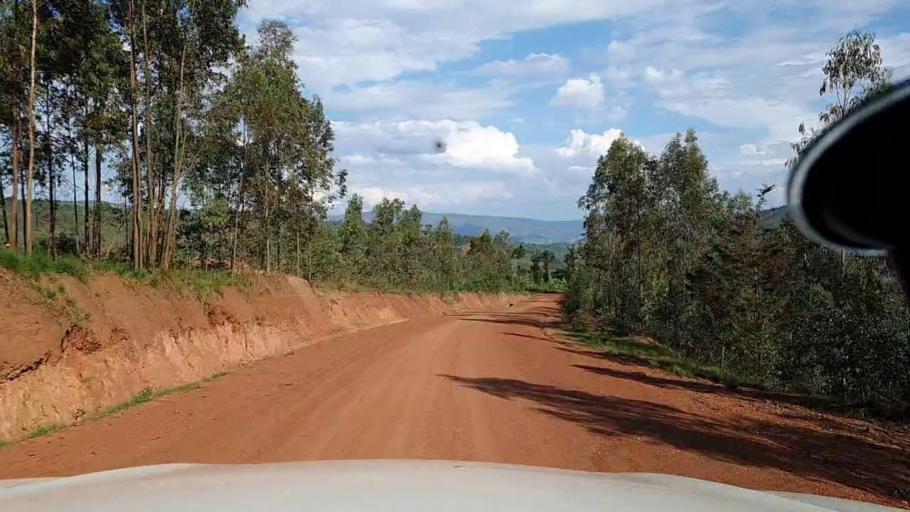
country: RW
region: Kigali
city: Kigali
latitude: -1.8437
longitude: 29.8593
